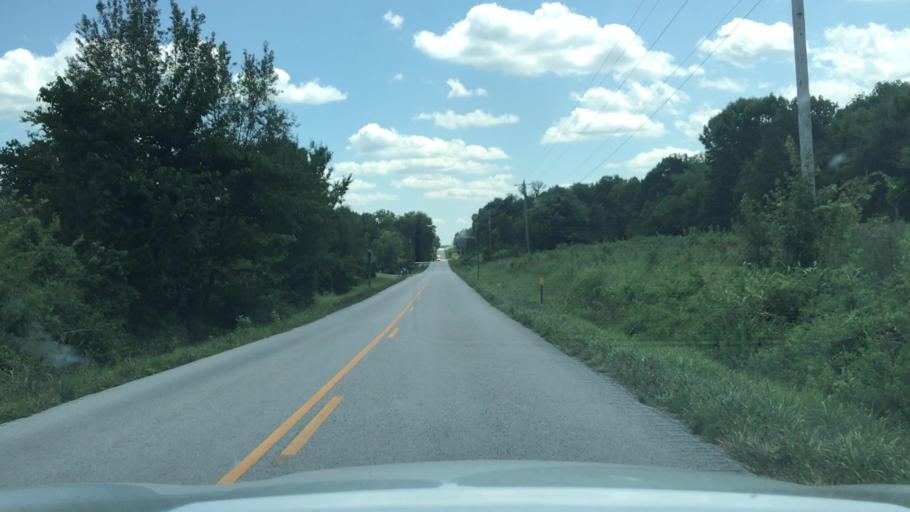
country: US
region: Kentucky
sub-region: Christian County
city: Hopkinsville
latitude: 37.0004
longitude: -87.3670
